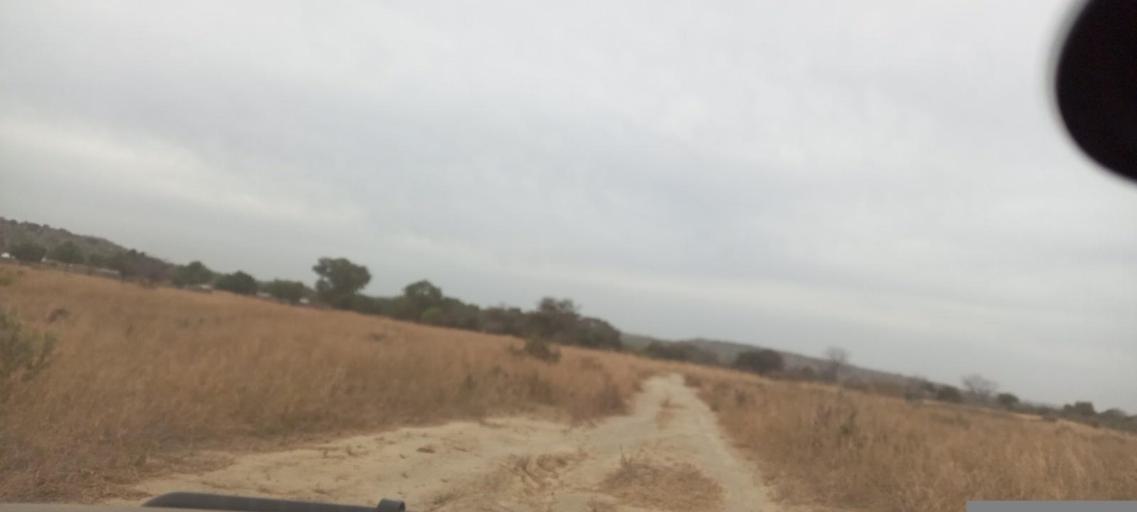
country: ML
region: Koulikoro
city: Kati
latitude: 12.7642
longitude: -8.4032
